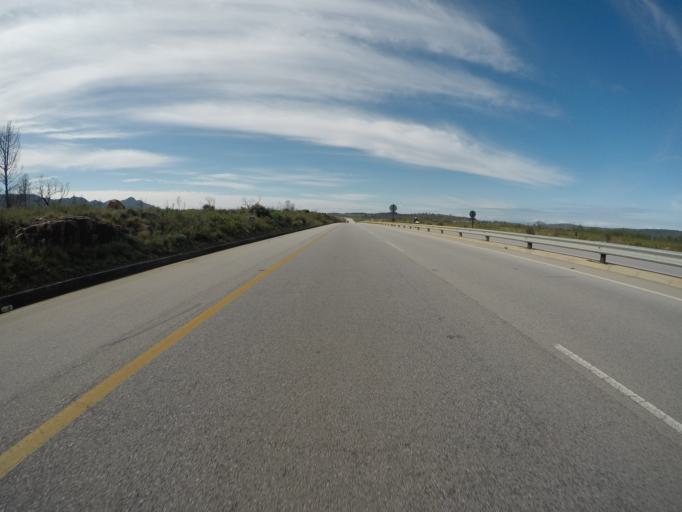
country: ZA
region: Eastern Cape
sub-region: Nelson Mandela Bay Metropolitan Municipality
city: Uitenhage
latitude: -33.9058
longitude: 25.1889
